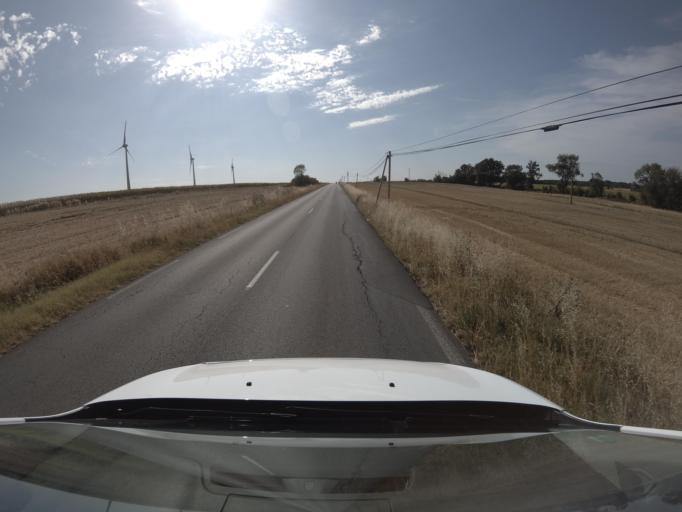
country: FR
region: Poitou-Charentes
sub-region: Departement des Deux-Sevres
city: Mauze-Thouarsais
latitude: 46.9986
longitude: -0.2724
